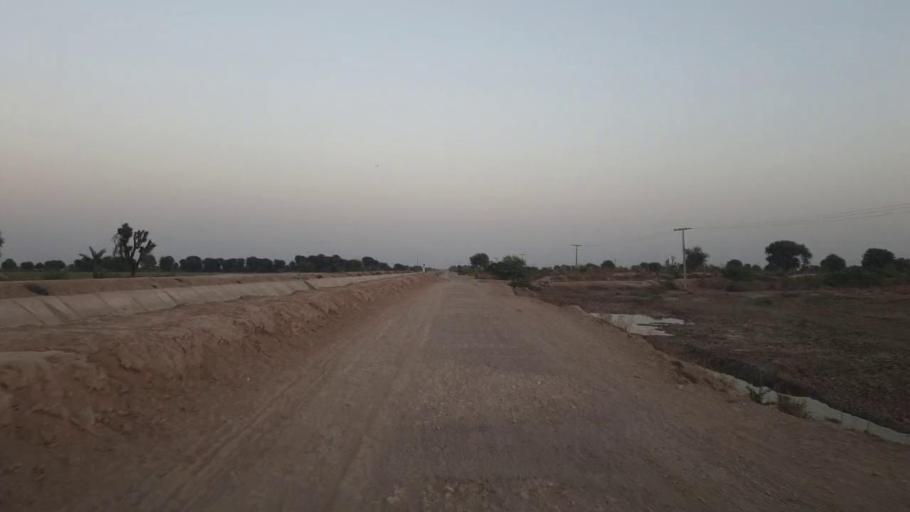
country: PK
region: Sindh
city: Umarkot
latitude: 25.4190
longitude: 69.6692
